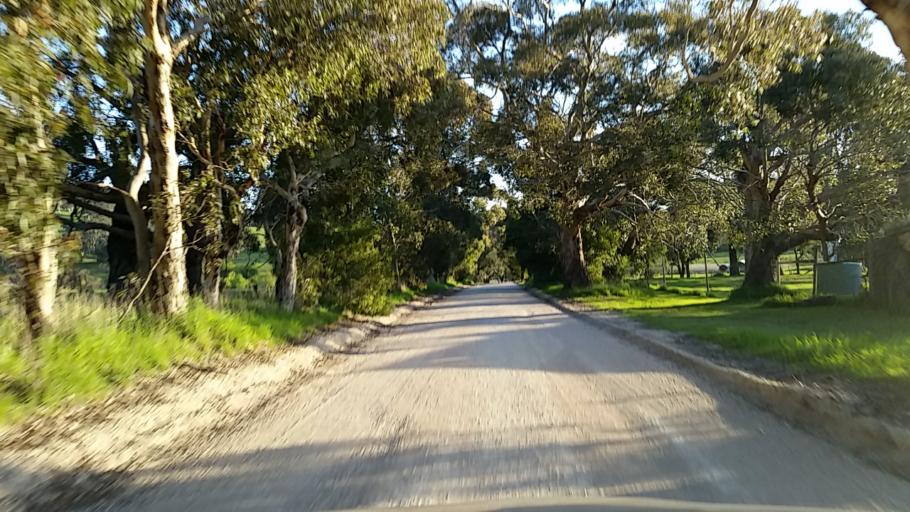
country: AU
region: South Australia
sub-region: Alexandrina
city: Mount Compass
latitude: -35.3189
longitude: 138.6700
